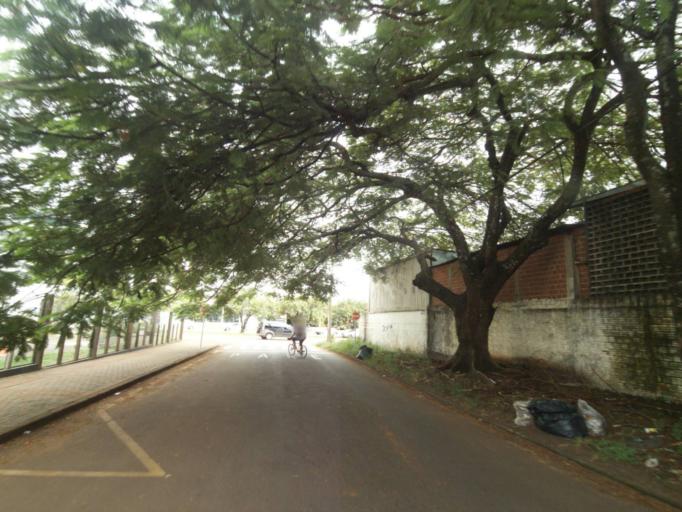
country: BR
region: Parana
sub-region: Campo Mourao
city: Campo Mourao
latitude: -24.0269
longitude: -52.3645
